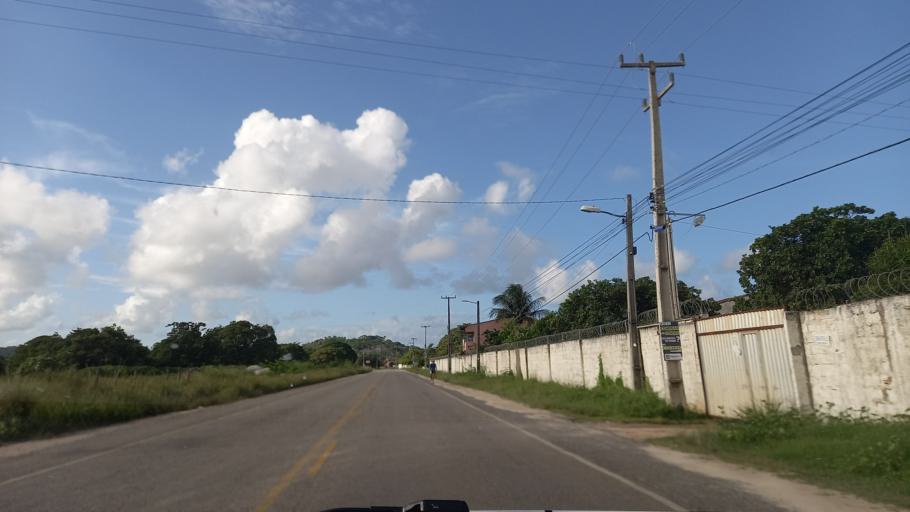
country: BR
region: Pernambuco
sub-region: Tamandare
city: Tamandare
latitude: -8.7210
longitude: -35.0951
